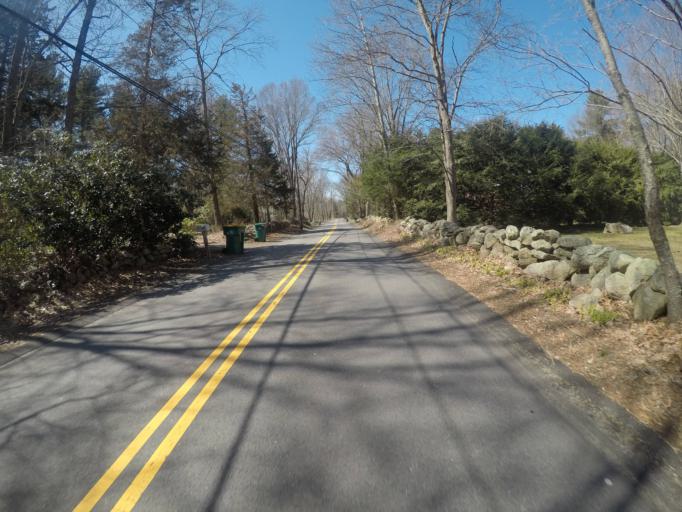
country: US
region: Massachusetts
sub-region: Bristol County
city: Easton
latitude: 42.0092
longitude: -71.1482
